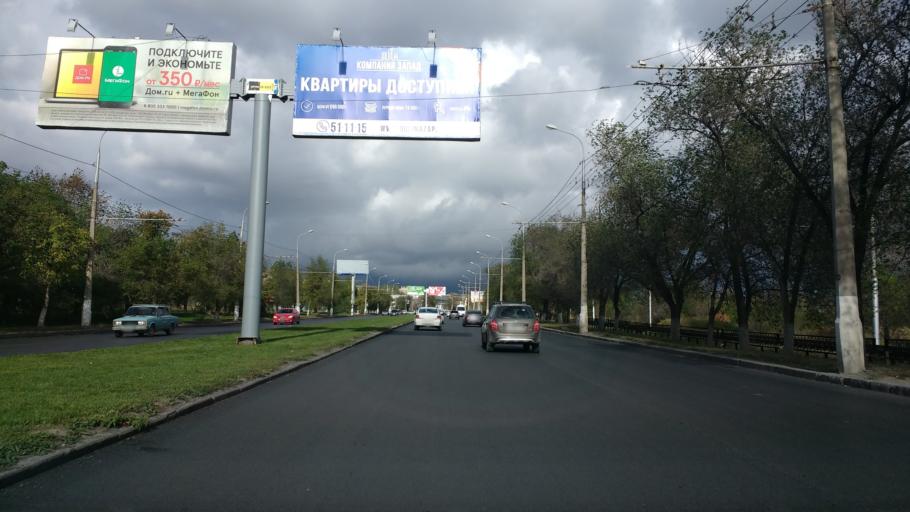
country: RU
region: Volgograd
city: Krasnoslobodsk
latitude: 48.7685
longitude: 44.5647
